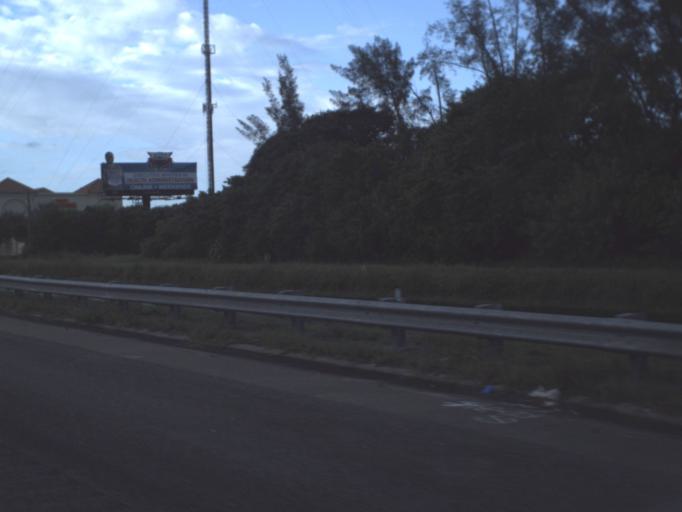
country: US
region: Florida
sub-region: Palm Beach County
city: Boca Del Mar
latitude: 26.3726
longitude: -80.1710
